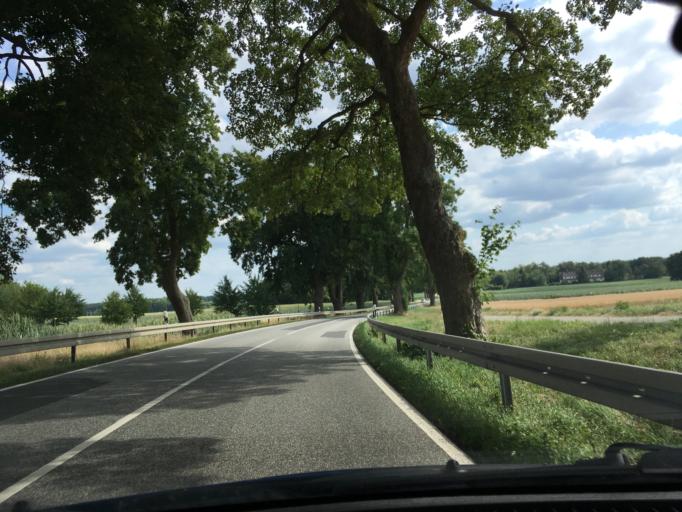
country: DE
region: Mecklenburg-Vorpommern
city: Lubtheen
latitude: 53.3731
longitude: 11.0848
